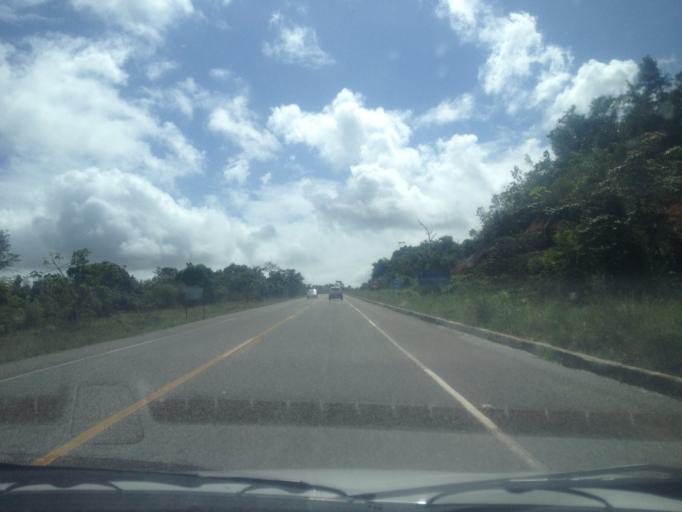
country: BR
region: Bahia
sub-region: Conde
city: Conde
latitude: -11.9770
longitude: -37.6751
